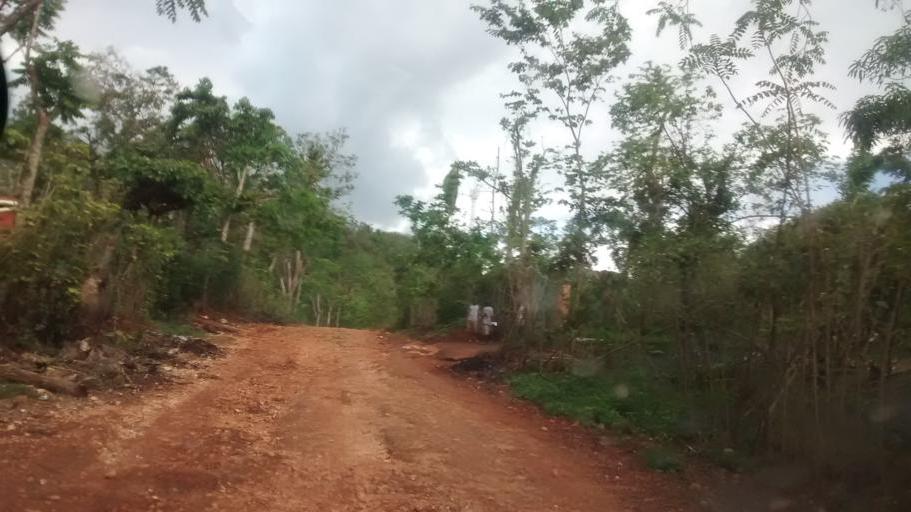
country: HT
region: Grandans
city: Corail
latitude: 18.5190
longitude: -73.7888
